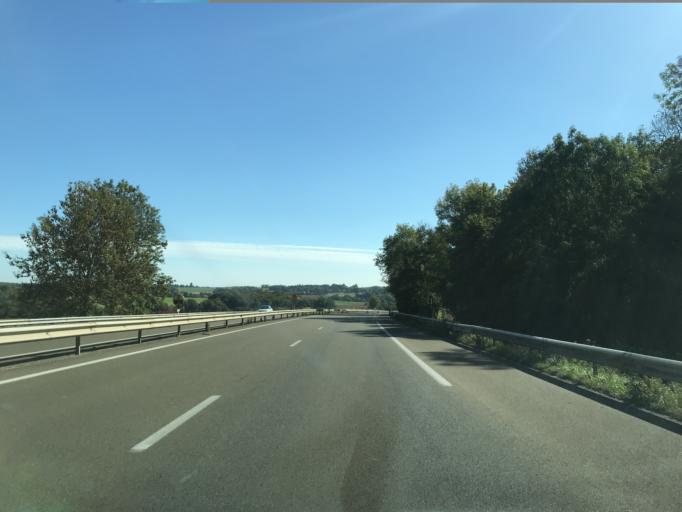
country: FR
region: Ile-de-France
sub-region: Departement de Seine-et-Marne
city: Bouleurs
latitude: 48.8942
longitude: 2.8948
